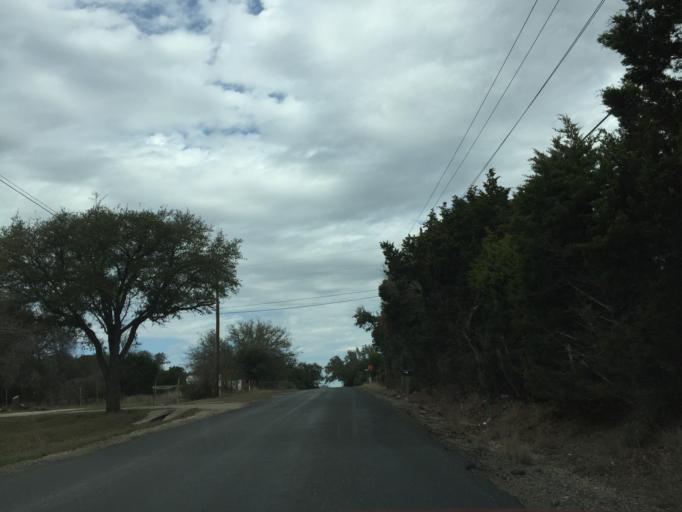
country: US
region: Texas
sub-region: Burnet County
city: Bertram
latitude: 30.7239
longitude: -97.9319
